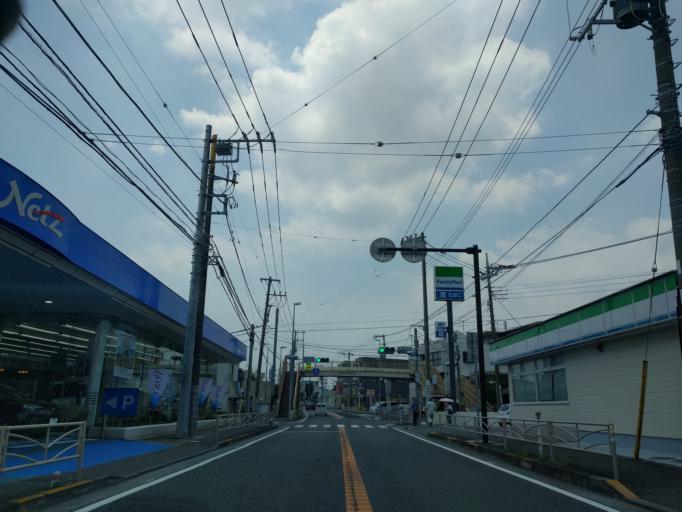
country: JP
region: Kanagawa
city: Minami-rinkan
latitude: 35.4823
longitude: 139.5314
